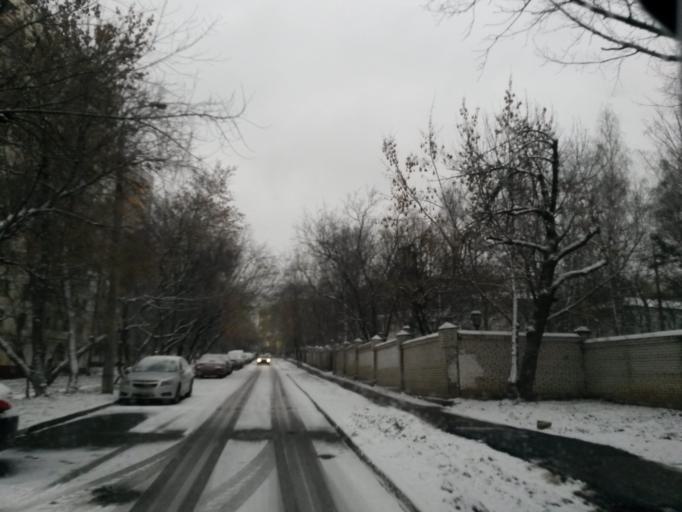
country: RU
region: Moskovskaya
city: Bol'shaya Setun'
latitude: 55.7188
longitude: 37.4347
